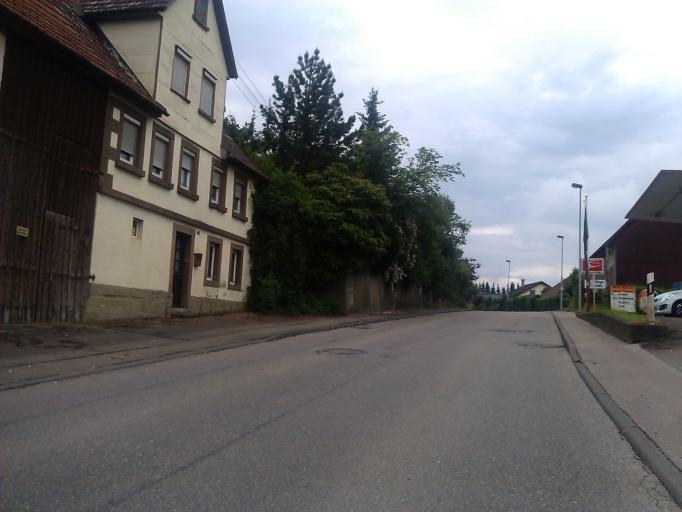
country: DE
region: Baden-Wuerttemberg
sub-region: Regierungsbezirk Stuttgart
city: Oberrot
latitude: 49.0032
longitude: 9.6800
